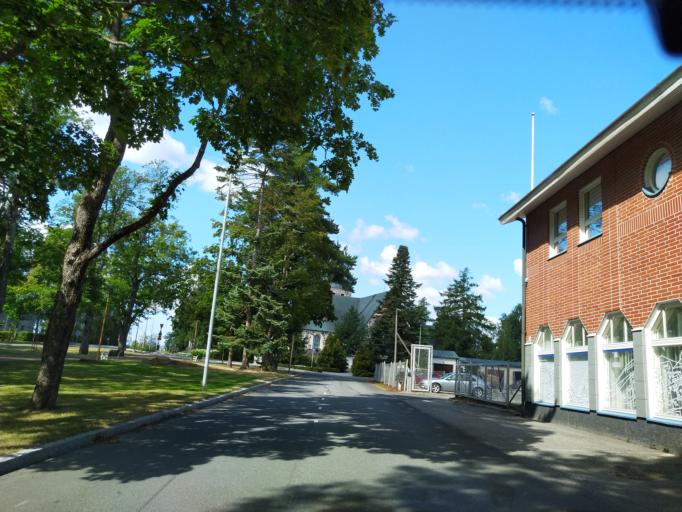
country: FI
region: Satakunta
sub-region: Pori
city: Huittinen
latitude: 61.1802
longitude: 22.6956
